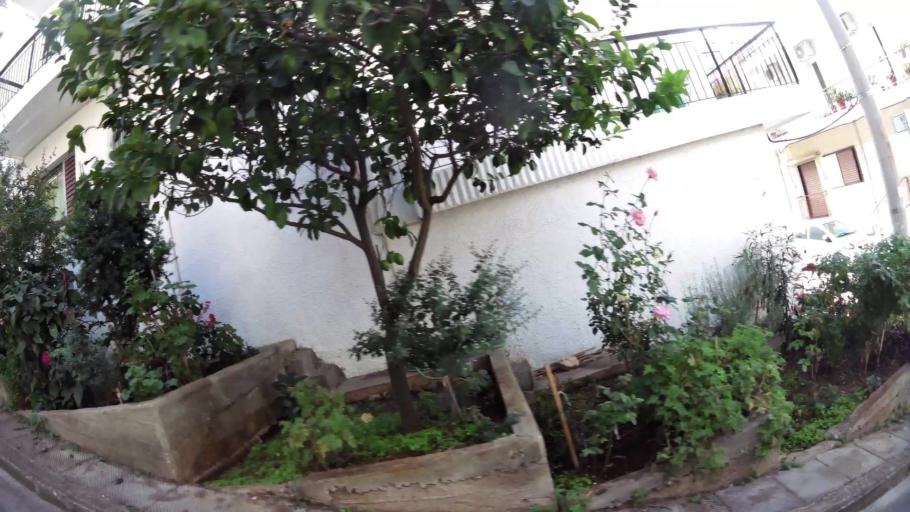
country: GR
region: Attica
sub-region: Nomarchia Athinas
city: Ilioupoli
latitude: 37.9442
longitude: 23.7654
